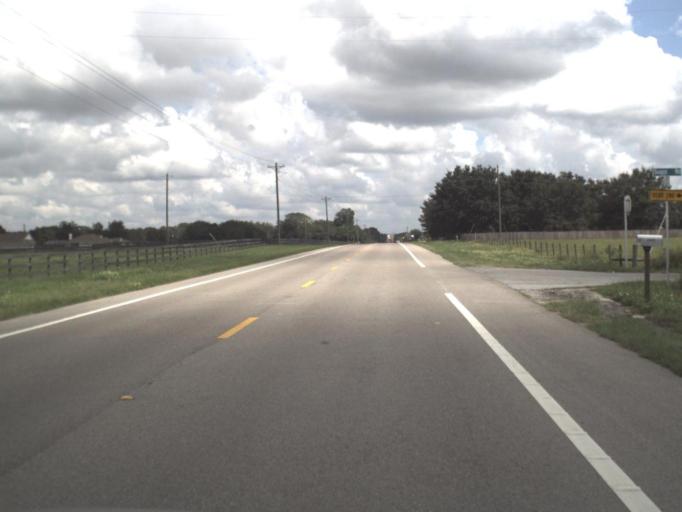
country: US
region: Florida
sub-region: Sarasota County
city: The Meadows
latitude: 27.4766
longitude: -82.2869
